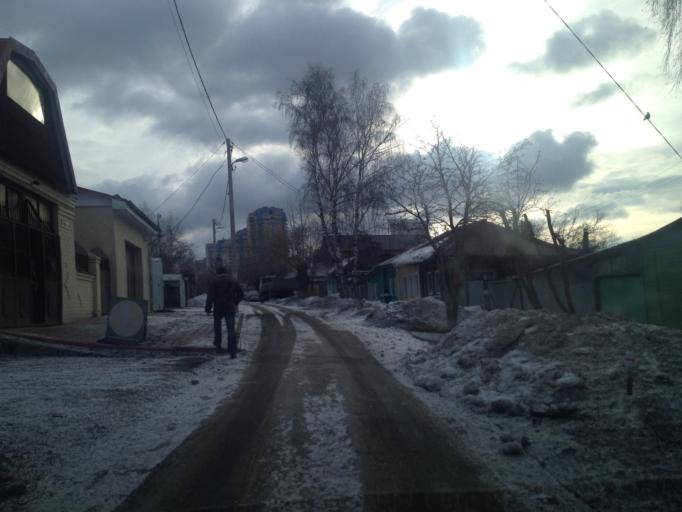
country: RU
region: Sverdlovsk
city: Yekaterinburg
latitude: 56.8038
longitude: 60.5914
